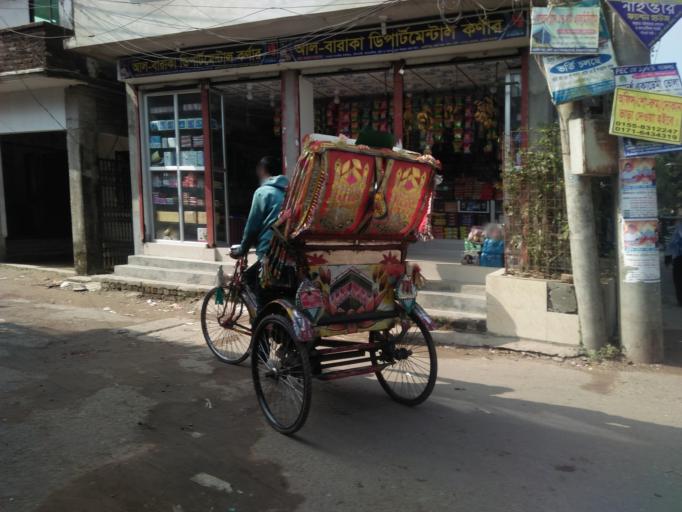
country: BD
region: Barisal
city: Bhola
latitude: 22.6850
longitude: 90.6429
